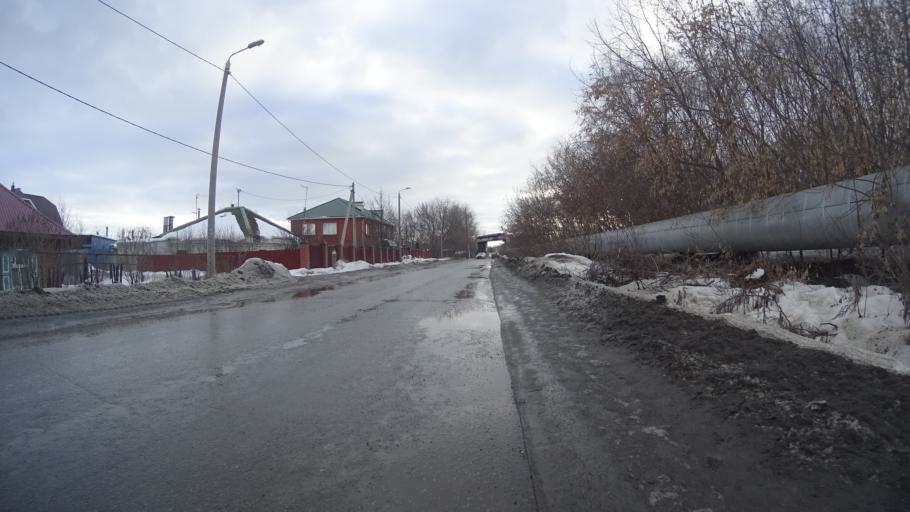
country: RU
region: Chelyabinsk
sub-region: Gorod Chelyabinsk
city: Chelyabinsk
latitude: 55.1369
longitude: 61.3931
